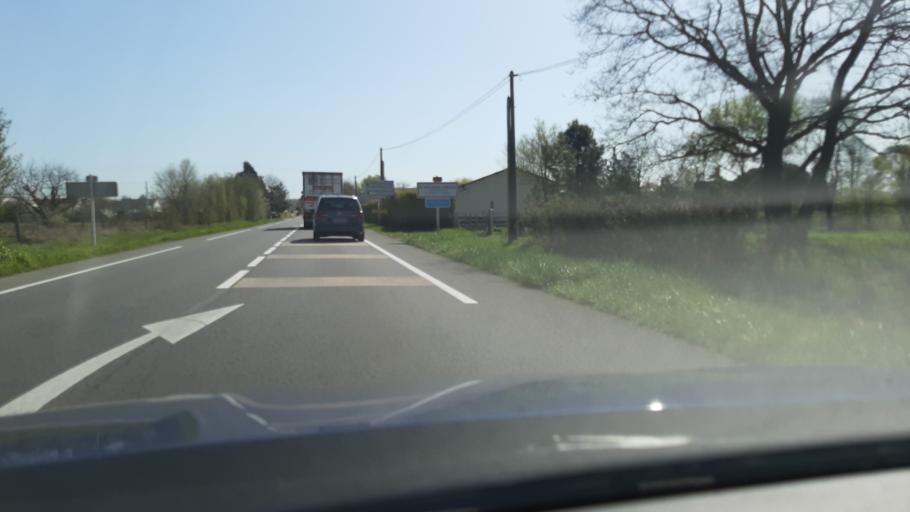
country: FR
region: Pays de la Loire
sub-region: Departement de Maine-et-Loire
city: Ecouflant
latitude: 47.5186
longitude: -0.4847
